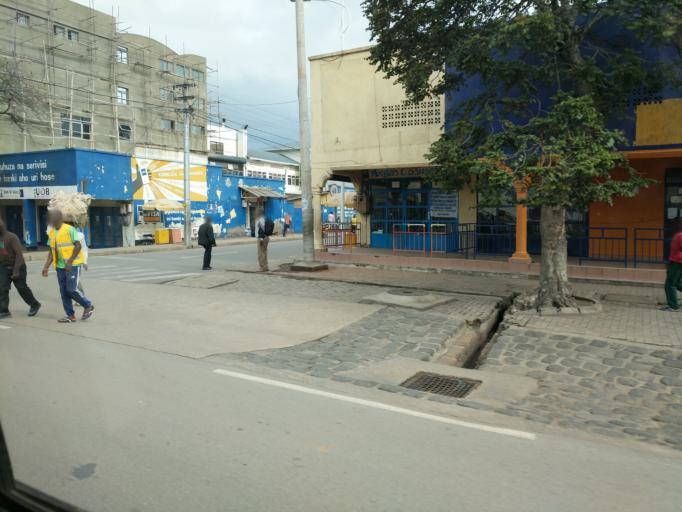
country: RW
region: Northern Province
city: Musanze
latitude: -1.5090
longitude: 29.6431
